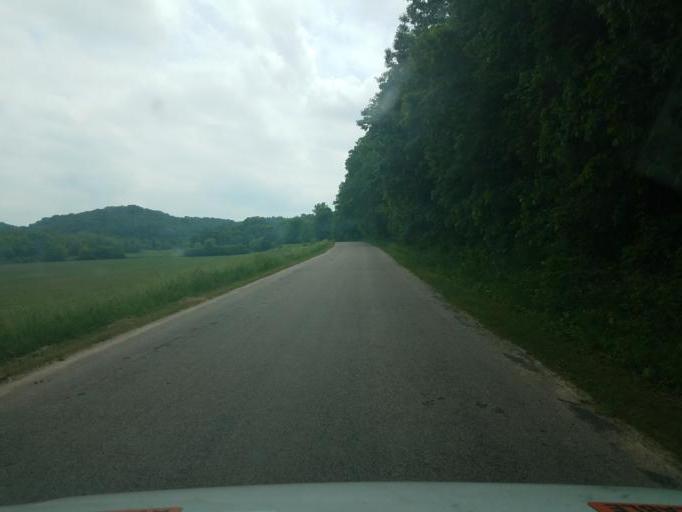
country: US
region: Wisconsin
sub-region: Vernon County
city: Hillsboro
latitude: 43.6040
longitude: -90.3694
